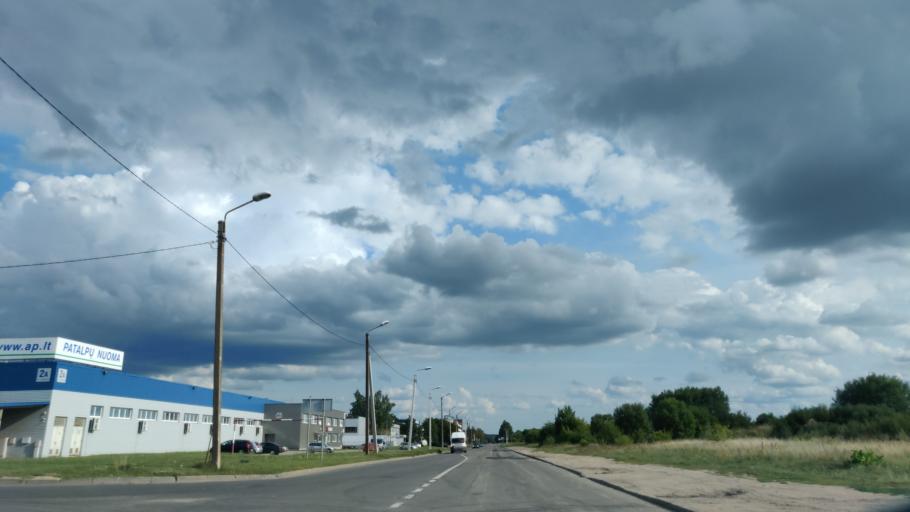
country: LT
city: Baltoji Voke
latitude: 54.6291
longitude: 25.1373
